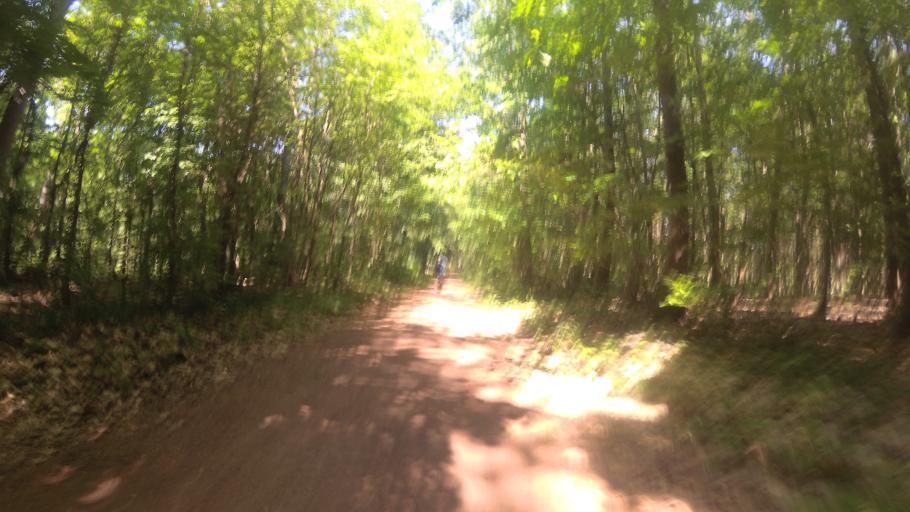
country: DE
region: Saarland
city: Beckingen
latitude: 49.4023
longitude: 6.7384
